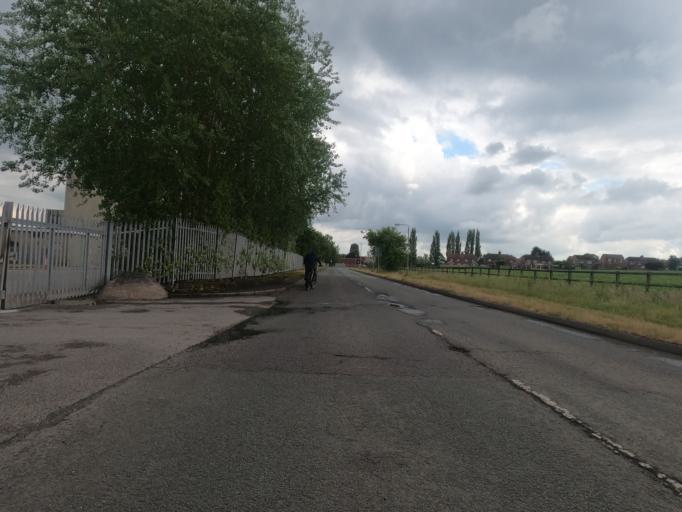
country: GB
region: England
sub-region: Cheshire West and Chester
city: Winsford
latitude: 53.2125
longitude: -2.5230
